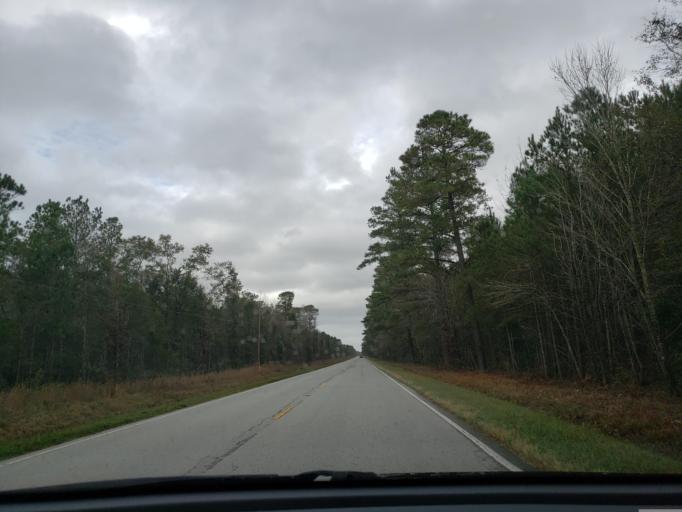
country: US
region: North Carolina
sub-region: Onslow County
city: Jacksonville
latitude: 34.7205
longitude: -77.6152
